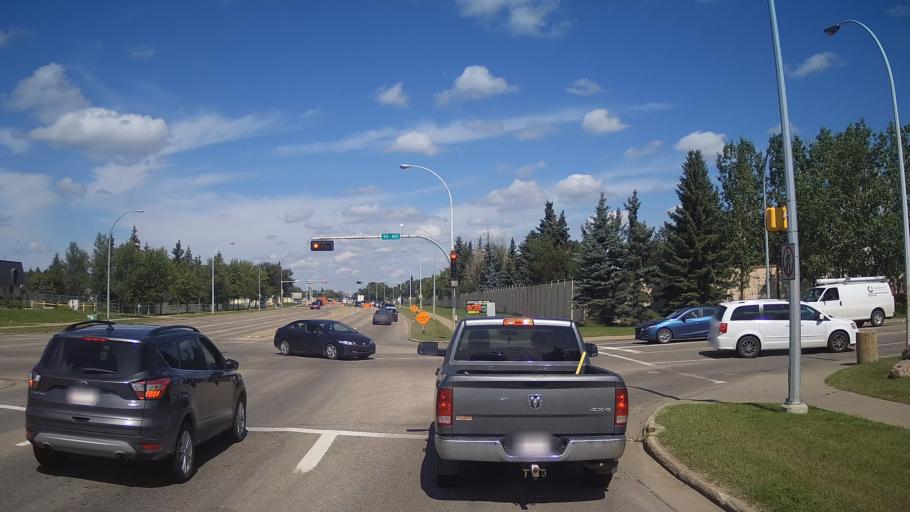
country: CA
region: Alberta
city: St. Albert
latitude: 53.5244
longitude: -113.6299
